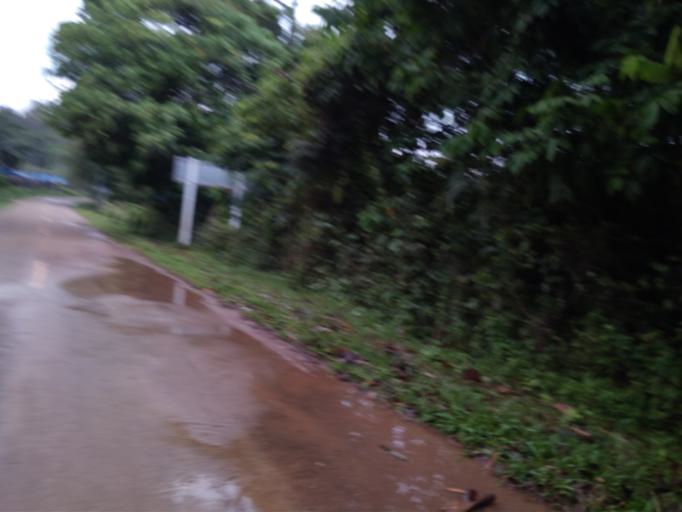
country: TH
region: Phangnga
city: Ko Yao
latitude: 8.1176
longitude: 98.6229
